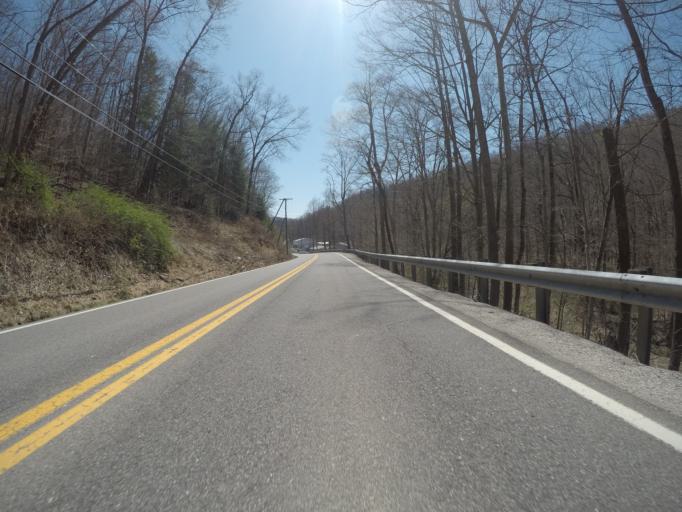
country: US
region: West Virginia
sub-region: Kanawha County
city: Pinch
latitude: 38.3897
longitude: -81.5591
